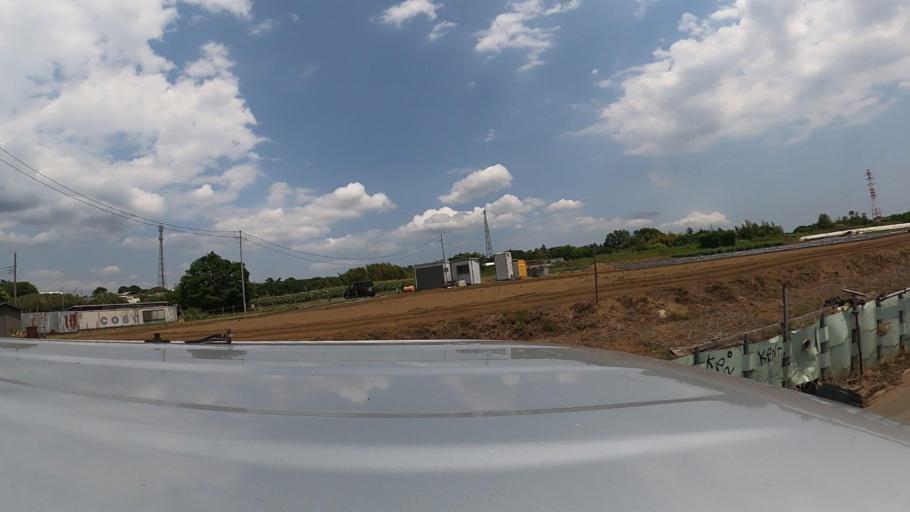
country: JP
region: Kanagawa
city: Chigasaki
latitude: 35.3865
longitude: 139.4190
